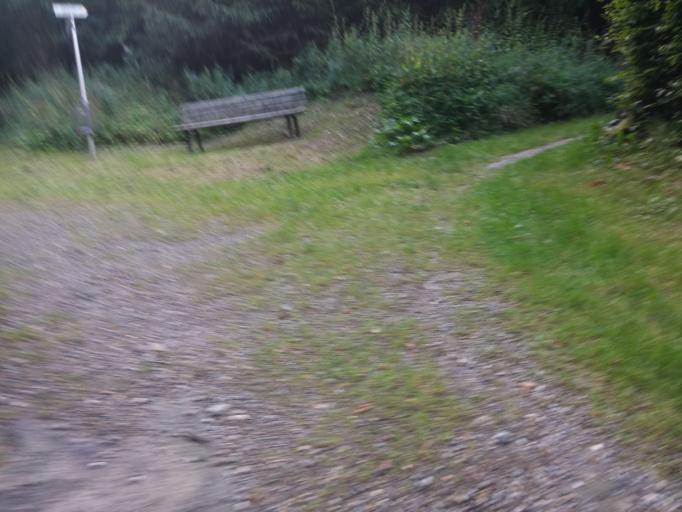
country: DE
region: Bavaria
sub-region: Swabia
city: Woringen
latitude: 47.8781
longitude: 10.2126
